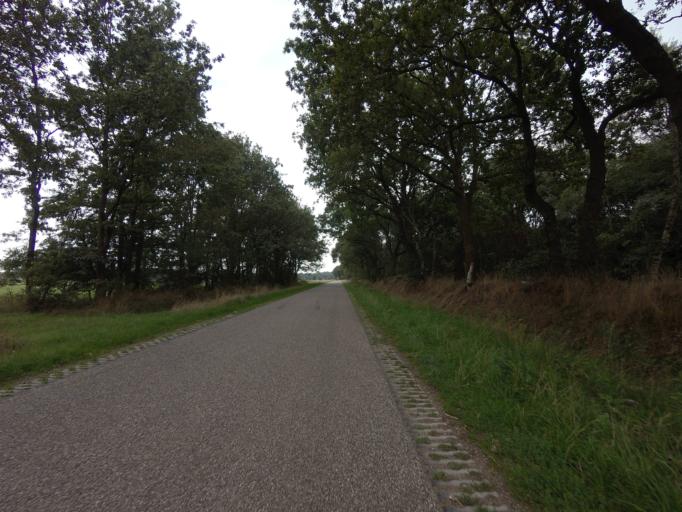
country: NL
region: Drenthe
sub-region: Gemeente Tynaarlo
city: Vries
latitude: 53.0418
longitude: 6.5987
